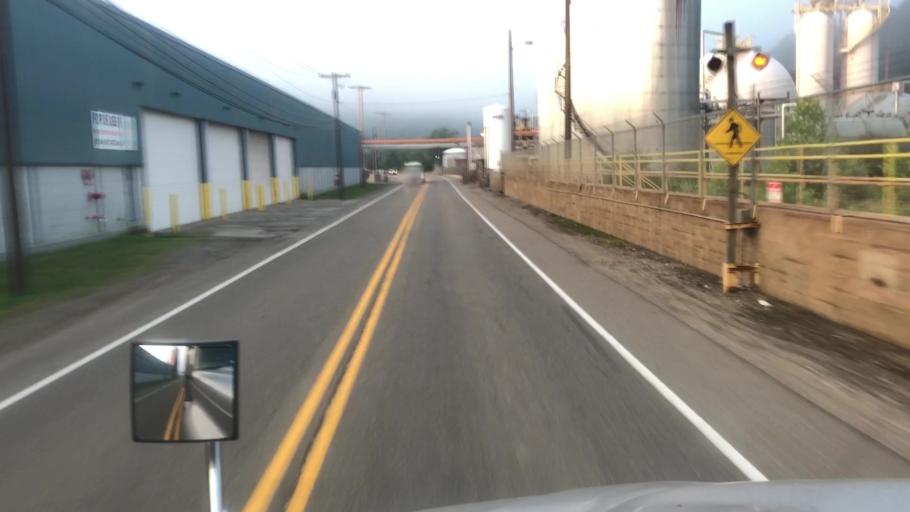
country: US
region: Pennsylvania
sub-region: Venango County
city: Hasson Heights
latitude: 41.4545
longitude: -79.6897
